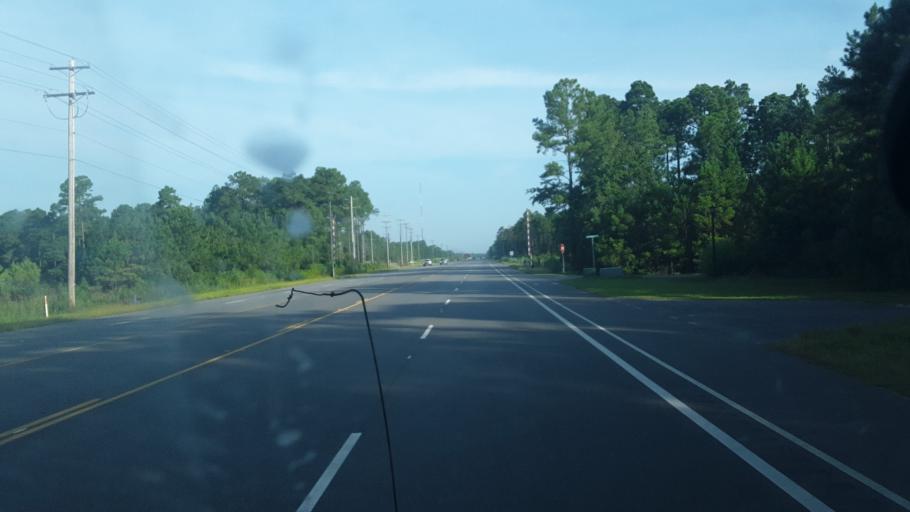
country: US
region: South Carolina
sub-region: Horry County
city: Myrtle Beach
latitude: 33.7713
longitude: -78.8687
